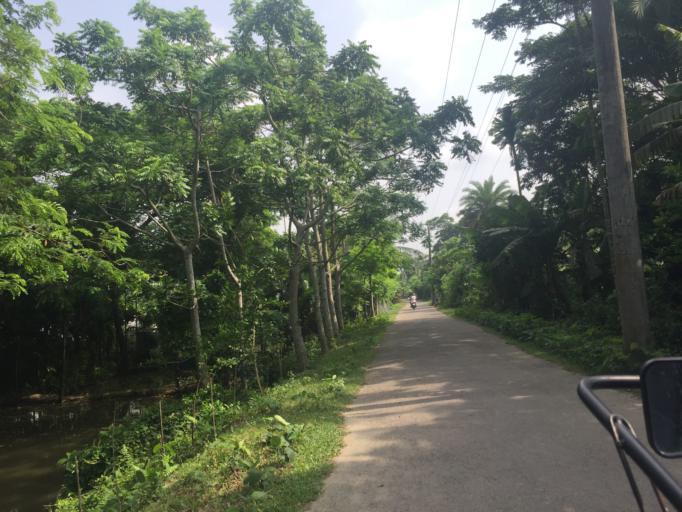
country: BD
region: Barisal
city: Mathba
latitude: 22.2312
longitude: 89.9157
